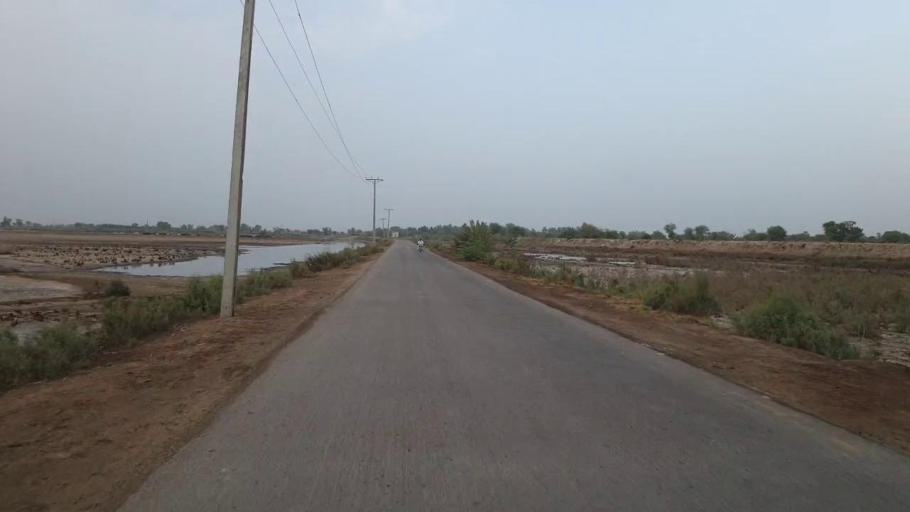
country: PK
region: Sindh
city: Daur
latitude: 26.4306
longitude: 68.2649
